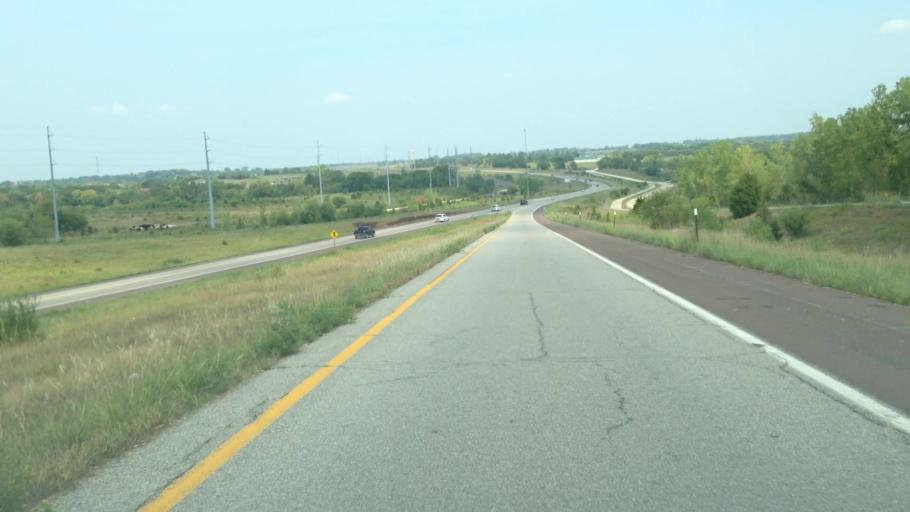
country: US
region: Kansas
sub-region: Douglas County
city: Lawrence
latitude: 38.9727
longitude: -95.3337
